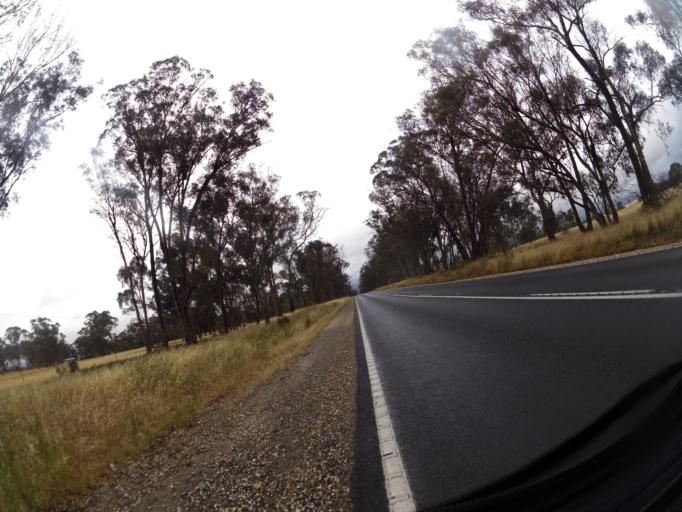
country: AU
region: Victoria
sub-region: Mount Alexander
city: Castlemaine
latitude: -37.0911
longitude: 144.1437
